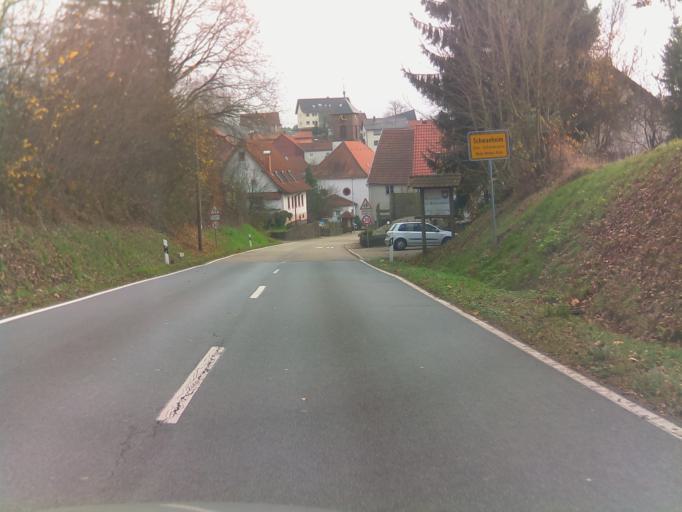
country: DE
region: Baden-Wuerttemberg
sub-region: Karlsruhe Region
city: Neunkirchen
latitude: 49.4034
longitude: 8.9721
